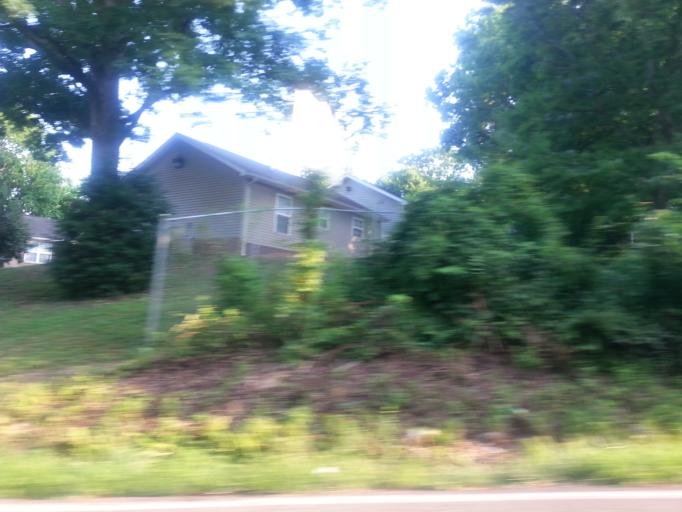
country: US
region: Tennessee
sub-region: Knox County
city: Knoxville
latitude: 36.0474
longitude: -83.9233
